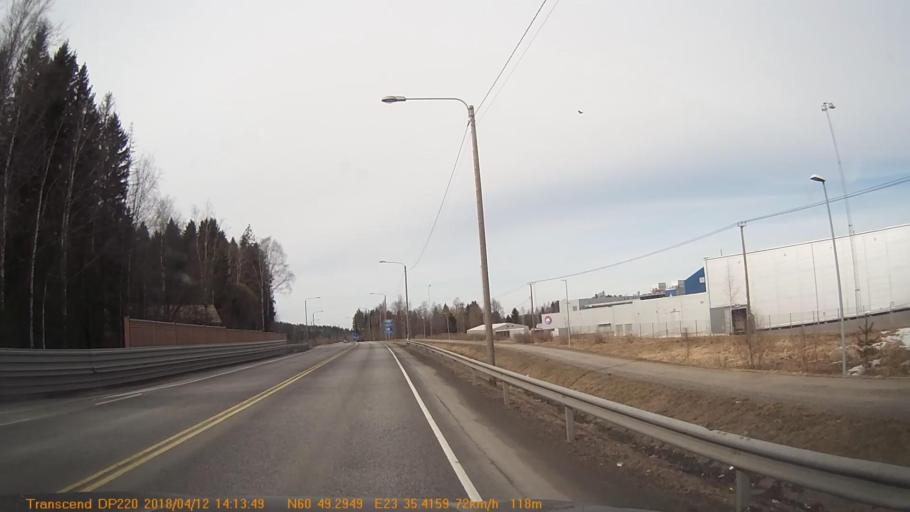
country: FI
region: Haeme
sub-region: Forssa
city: Forssa
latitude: 60.8219
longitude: 23.5900
